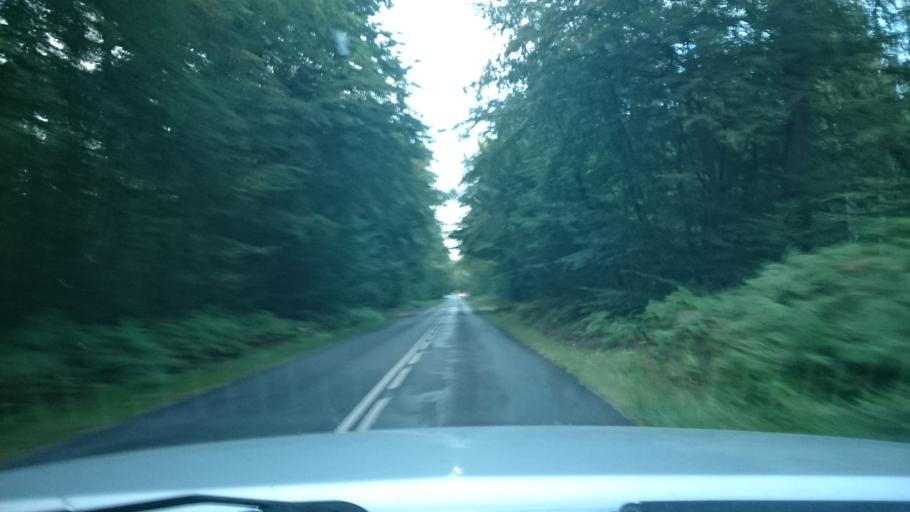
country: FR
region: Ile-de-France
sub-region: Departement de Seine-et-Marne
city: Bois-le-Roi
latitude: 48.4541
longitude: 2.7234
